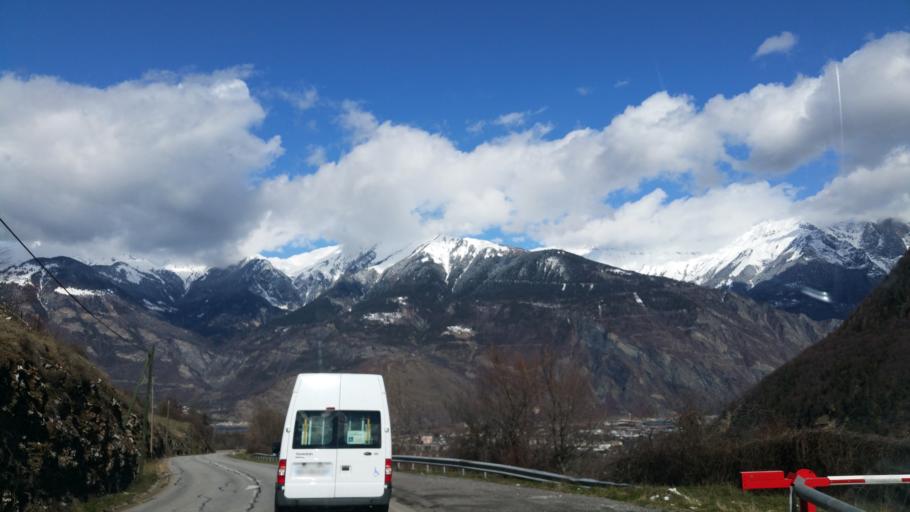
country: FR
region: Rhone-Alpes
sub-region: Departement de la Savoie
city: Saint-Jean-de-Maurienne
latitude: 45.2610
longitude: 6.3259
